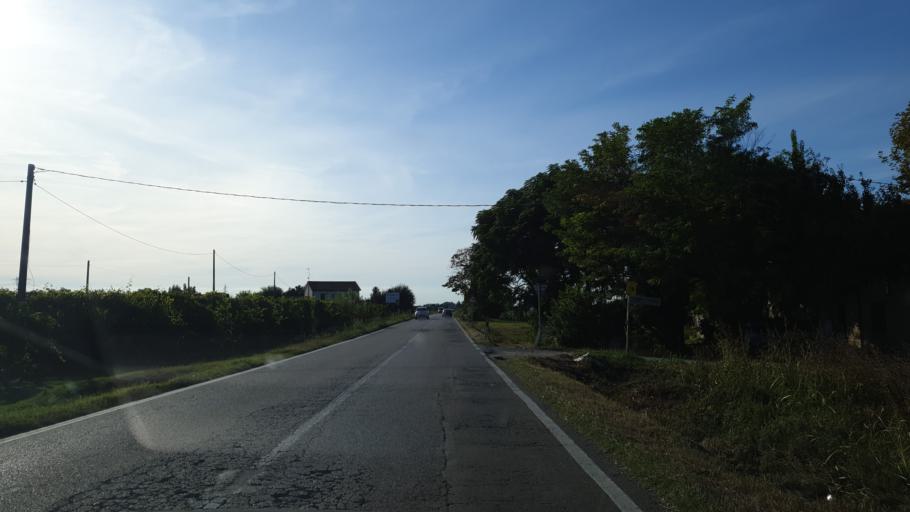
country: IT
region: Emilia-Romagna
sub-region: Provincia di Ravenna
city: Voltana
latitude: 44.5484
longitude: 11.9620
